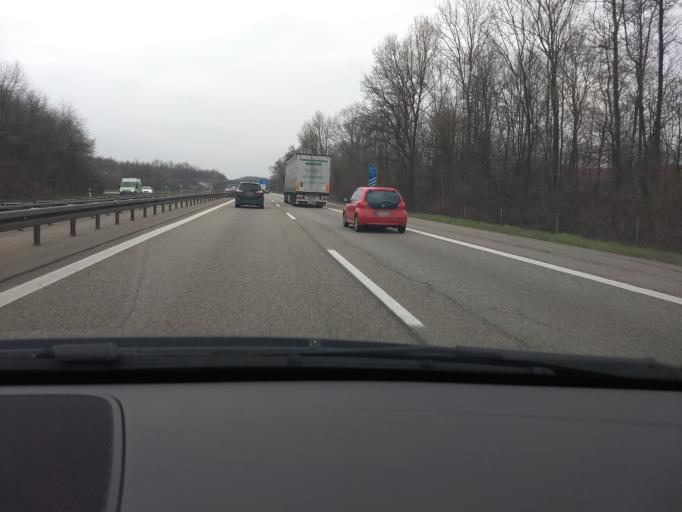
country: DE
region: Baden-Wuerttemberg
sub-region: Freiburg Region
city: Teningen
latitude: 48.1117
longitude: 7.7891
